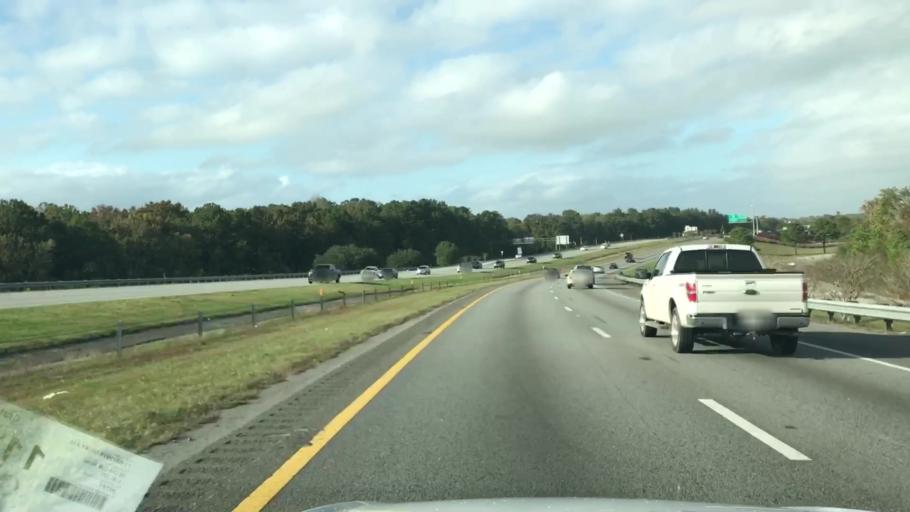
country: US
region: South Carolina
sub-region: Charleston County
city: North Charleston
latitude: 32.8646
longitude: -80.0267
